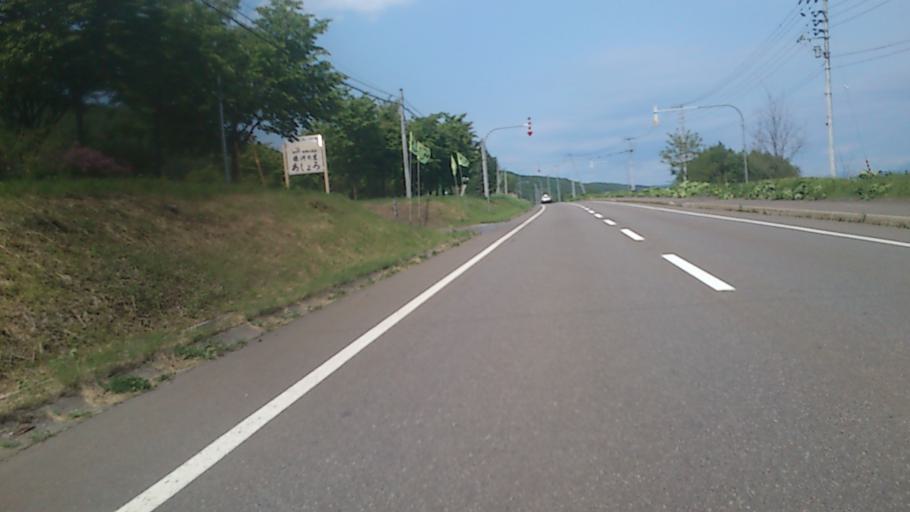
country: JP
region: Hokkaido
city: Otofuke
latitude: 43.2558
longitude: 143.5689
